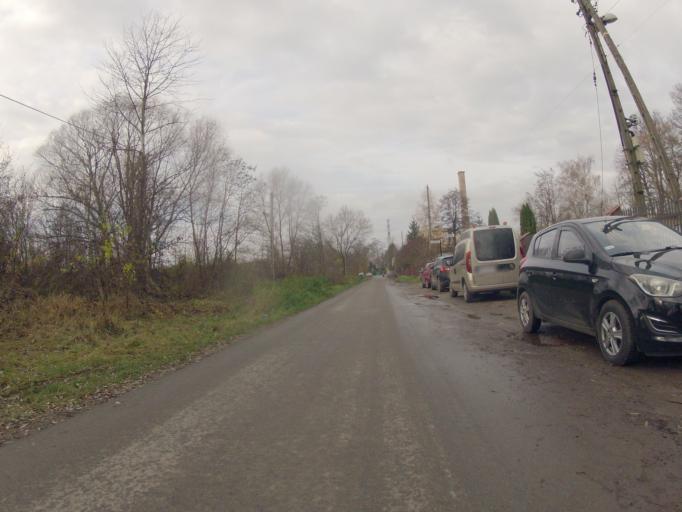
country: PL
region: Lesser Poland Voivodeship
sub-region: Powiat krakowski
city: Rzaska
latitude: 50.0809
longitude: 19.8512
